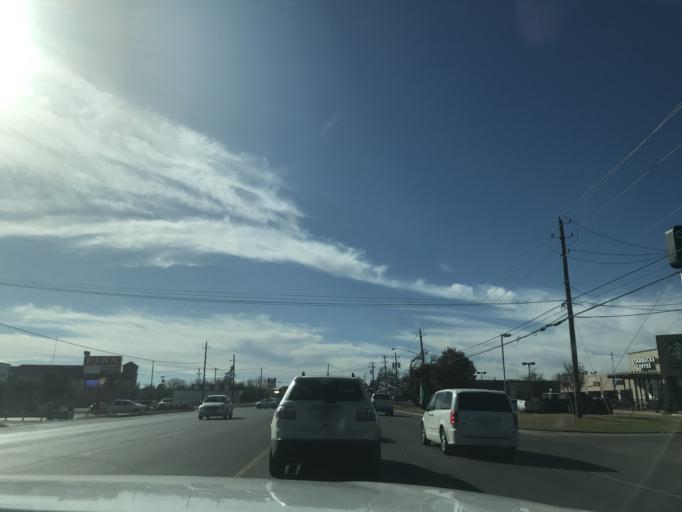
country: US
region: Texas
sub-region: Erath County
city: Stephenville
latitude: 32.2035
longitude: -98.2403
